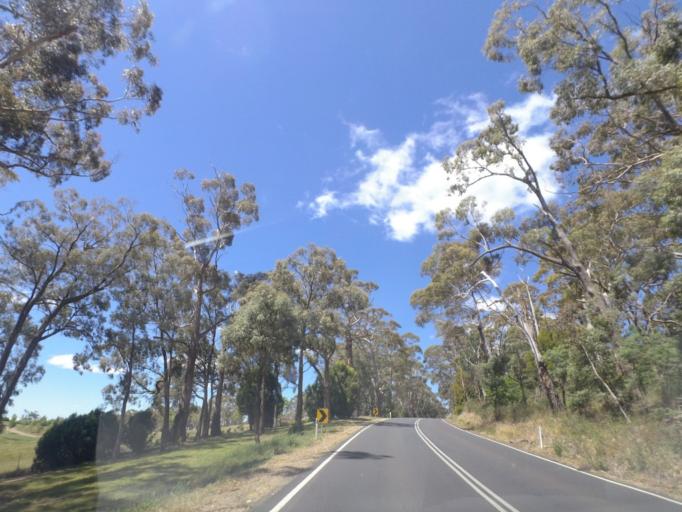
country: AU
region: Victoria
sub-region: Mount Alexander
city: Castlemaine
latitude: -37.2893
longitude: 144.2690
